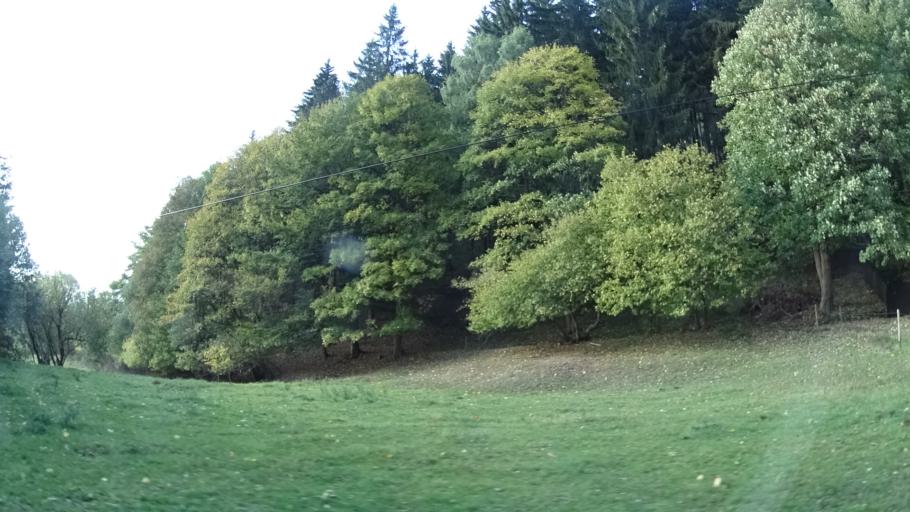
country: DE
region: Thuringia
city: Bermbach
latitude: 50.7171
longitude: 10.6206
